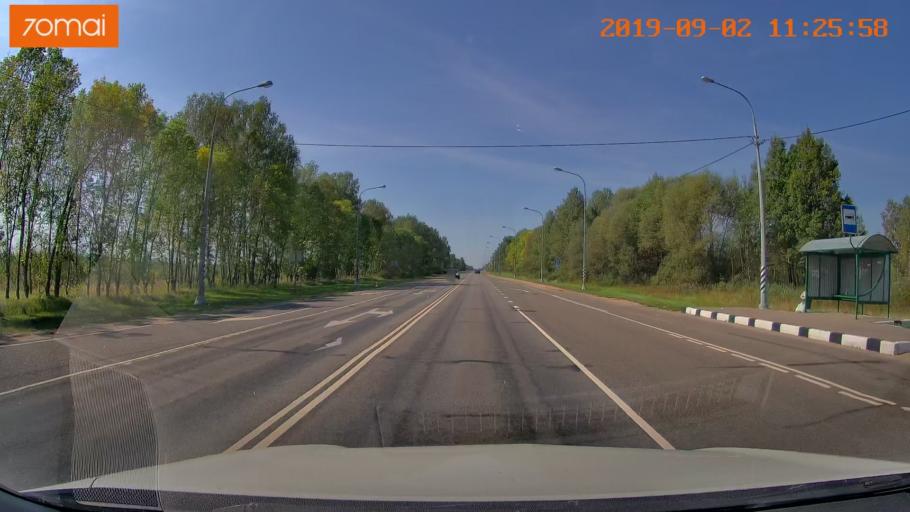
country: RU
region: Smolensk
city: Roslavl'
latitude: 53.9963
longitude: 32.9408
